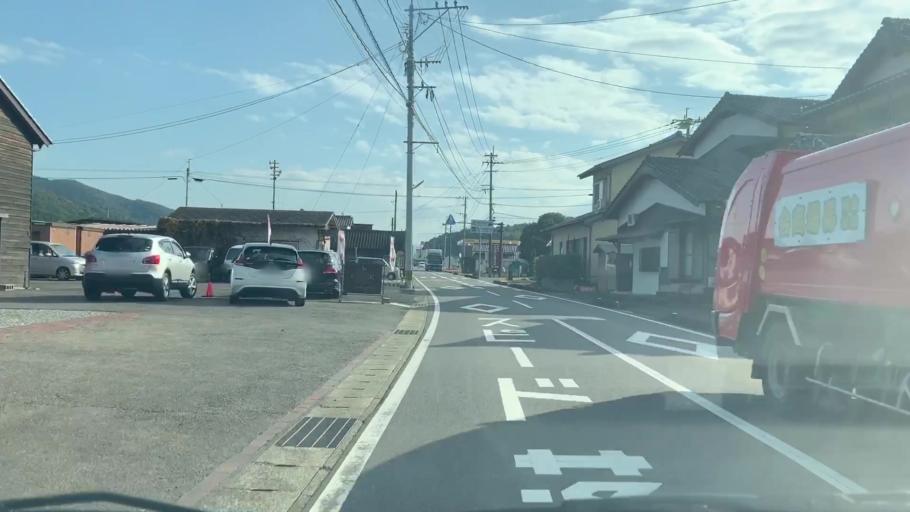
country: JP
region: Saga Prefecture
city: Takeocho-takeo
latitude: 33.1573
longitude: 130.0629
